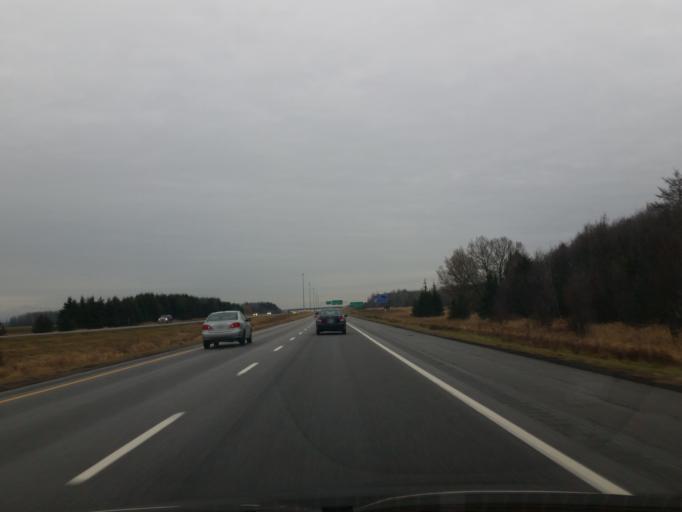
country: CA
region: Quebec
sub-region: Capitale-Nationale
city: Saint-Augustin-de-Desmaures
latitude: 46.7529
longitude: -71.4896
